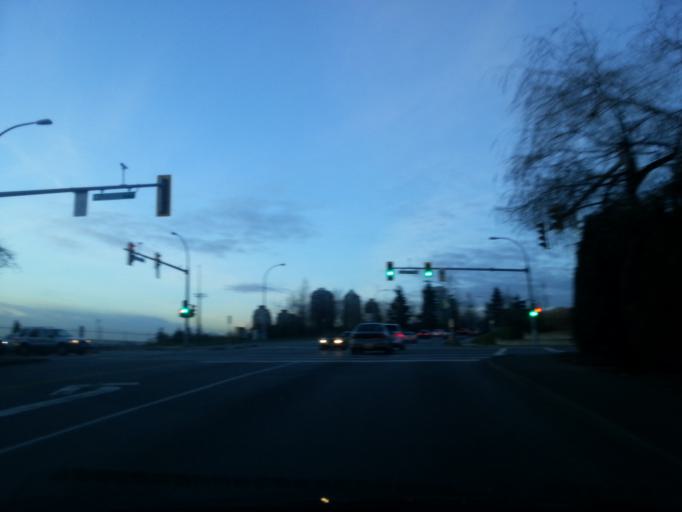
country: CA
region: British Columbia
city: New Westminster
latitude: 49.2056
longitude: -122.9518
